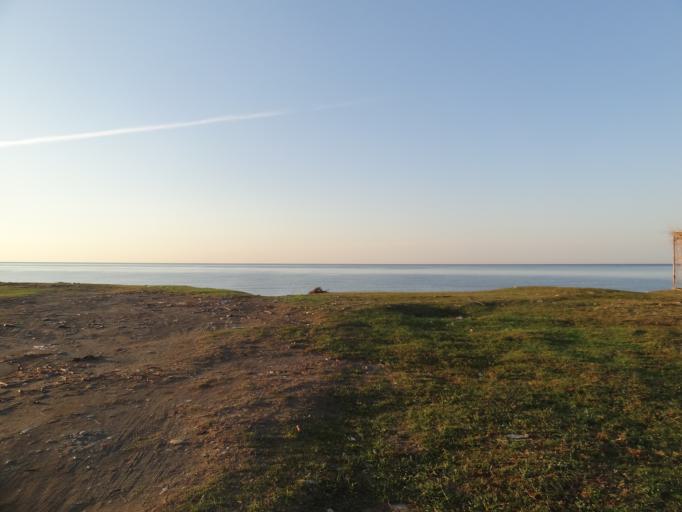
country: GE
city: Gantiadi
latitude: 43.3830
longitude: 40.0317
